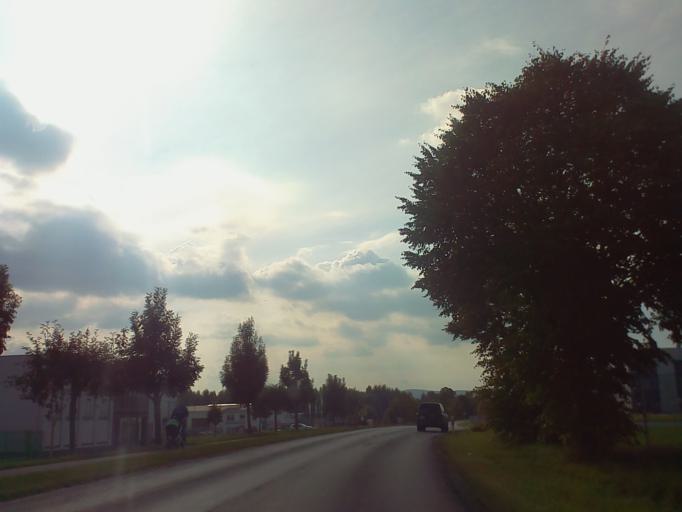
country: DE
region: Thuringia
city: Gerstungen
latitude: 50.9543
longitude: 10.0505
